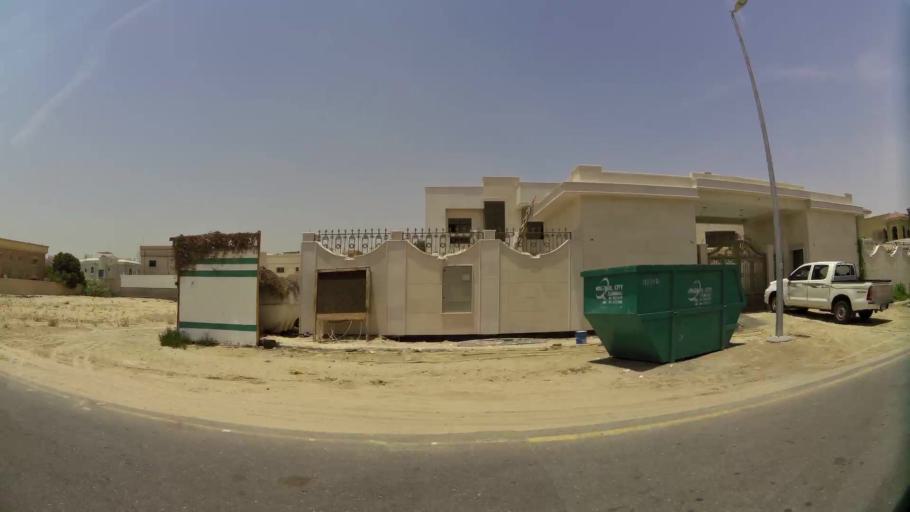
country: AE
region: Ash Shariqah
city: Sharjah
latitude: 25.2551
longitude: 55.4612
